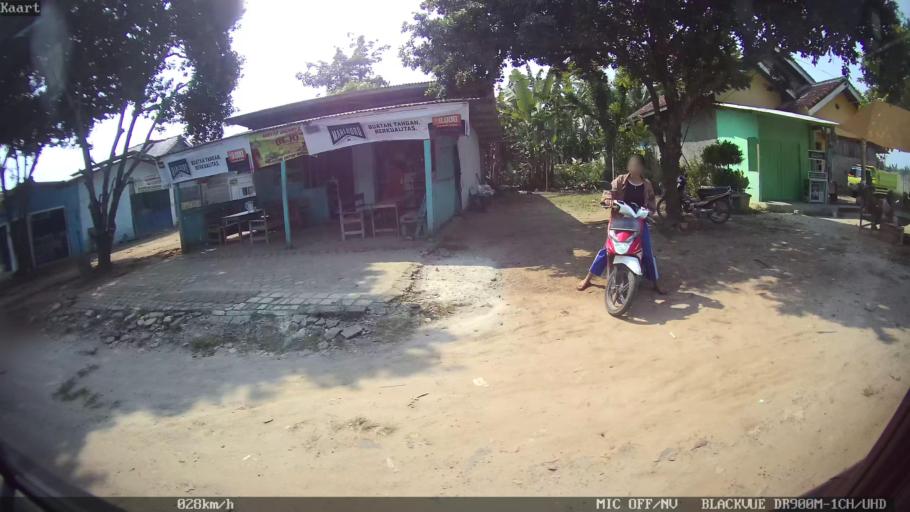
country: ID
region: Lampung
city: Natar
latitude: -5.3026
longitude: 105.2394
